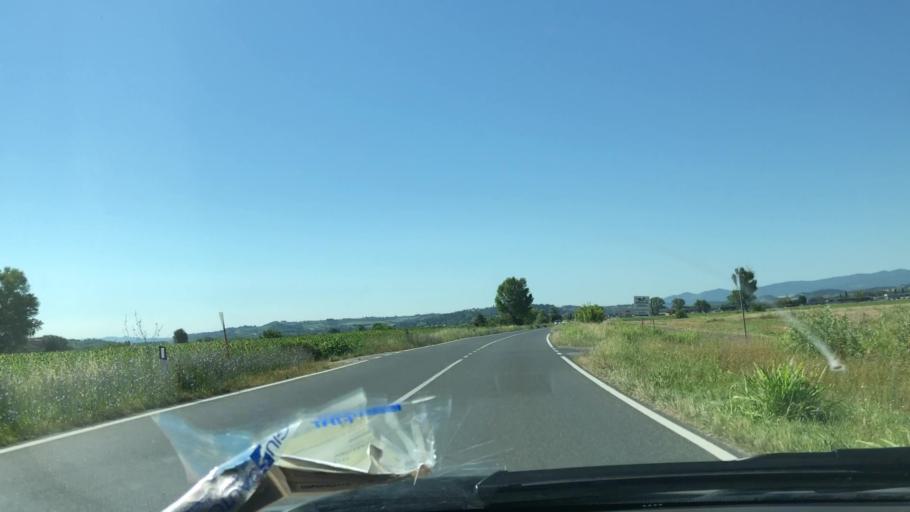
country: IT
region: Tuscany
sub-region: Province of Pisa
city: Forcoli
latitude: 43.5911
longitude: 10.7010
